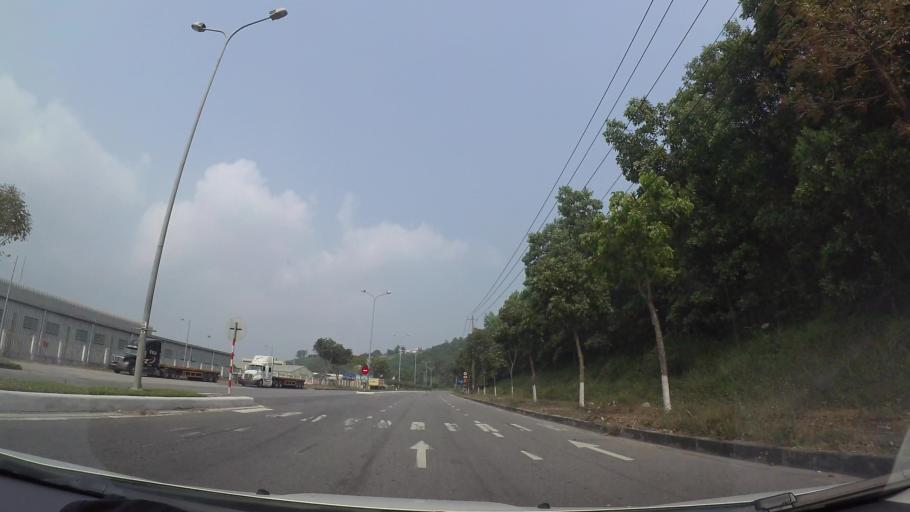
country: VN
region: Da Nang
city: Da Nang
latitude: 16.1172
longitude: 108.2312
